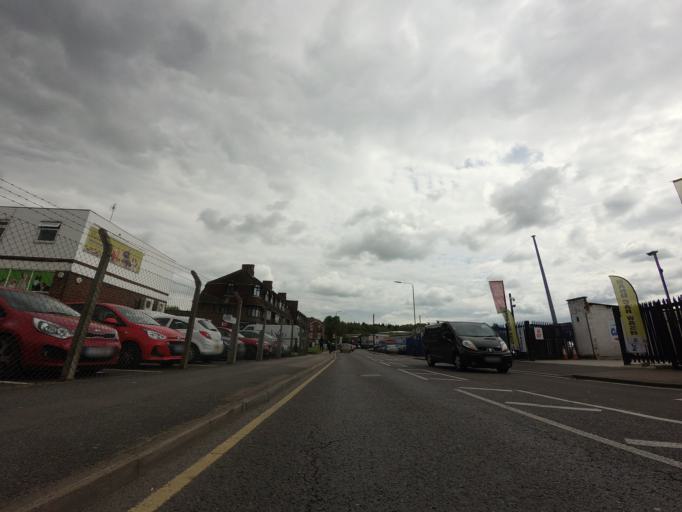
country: GB
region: England
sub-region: Greater London
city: Sidcup
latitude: 51.4170
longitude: 0.1224
